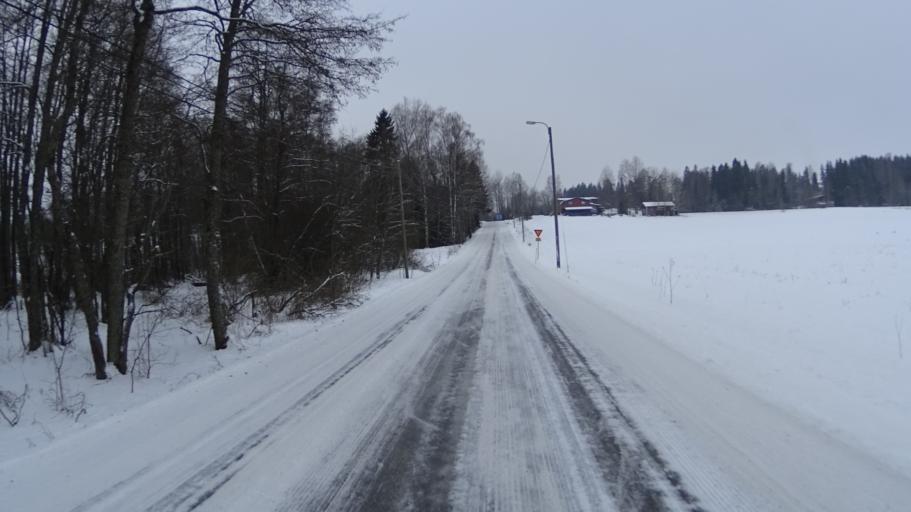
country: FI
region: Uusimaa
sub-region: Helsinki
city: Vihti
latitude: 60.3450
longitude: 24.1977
